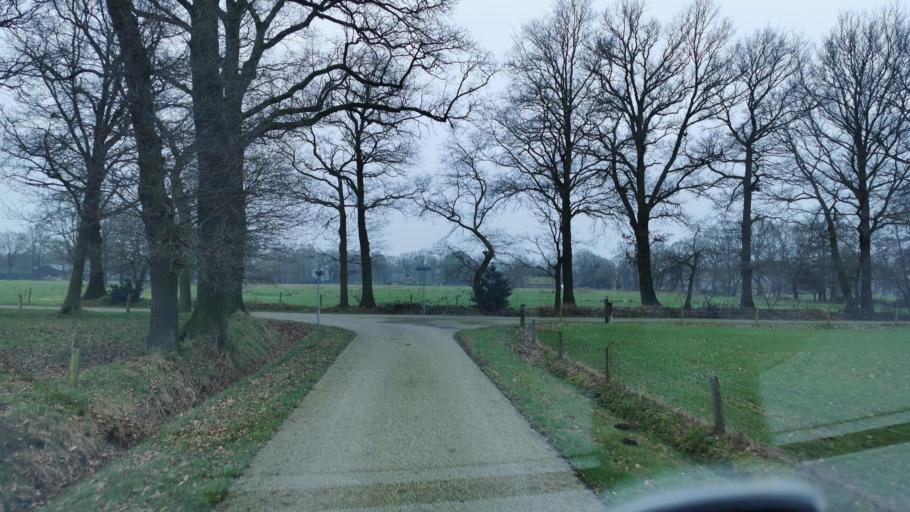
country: NL
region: Overijssel
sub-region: Gemeente Borne
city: Borne
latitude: 52.3425
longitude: 6.7880
